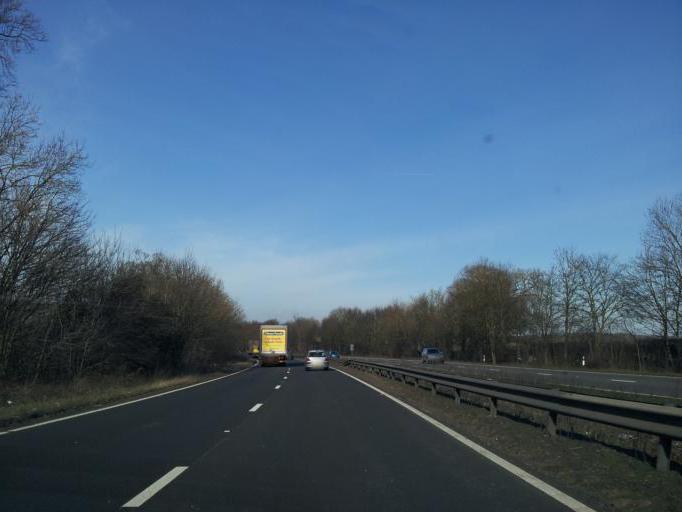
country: GB
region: England
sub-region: Lincolnshire
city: Grantham
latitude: 52.8505
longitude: -0.6269
